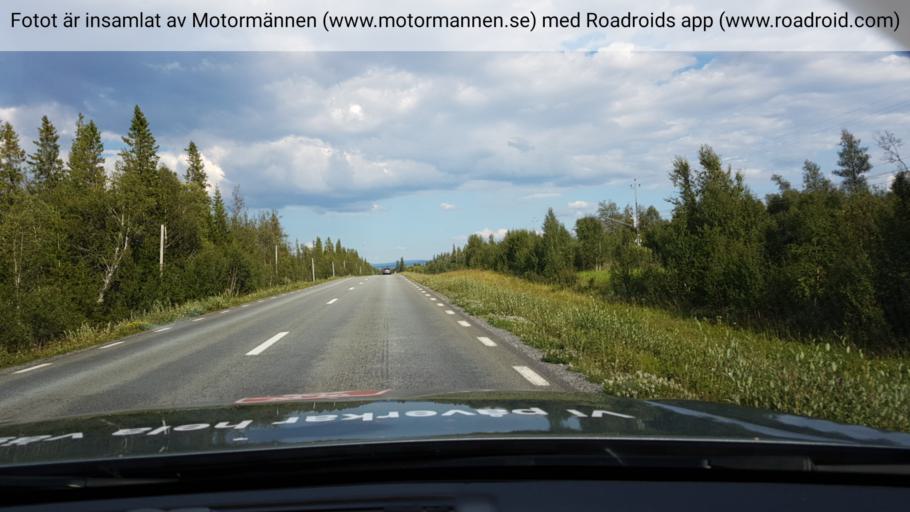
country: SE
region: Jaemtland
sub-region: Are Kommun
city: Are
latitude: 63.3089
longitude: 12.4584
